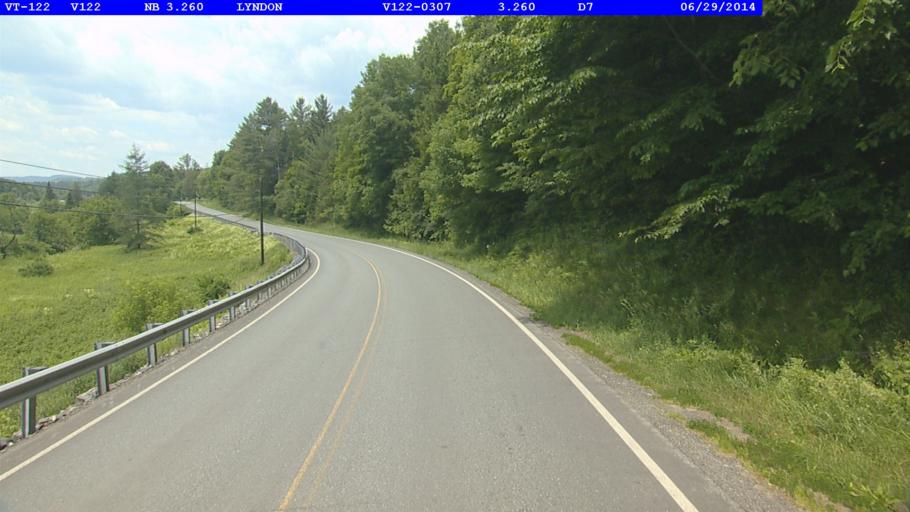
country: US
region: Vermont
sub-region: Caledonia County
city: Lyndonville
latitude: 44.5705
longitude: -72.0456
